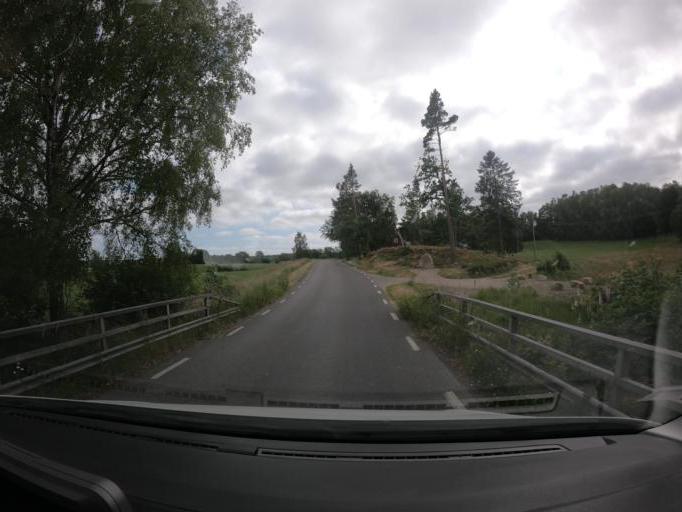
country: SE
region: Skane
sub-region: Hassleholms Kommun
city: Tormestorp
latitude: 56.1511
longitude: 13.6295
